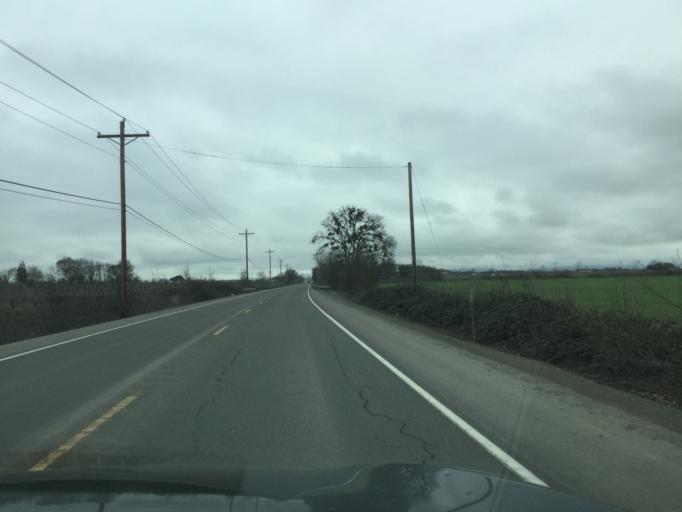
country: US
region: Oregon
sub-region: Jackson County
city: Central Point
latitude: 42.4277
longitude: -122.9520
